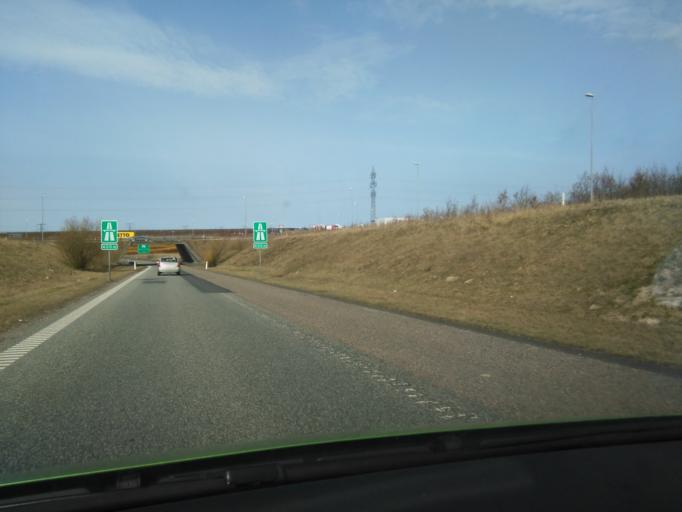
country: DK
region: Central Jutland
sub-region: Arhus Kommune
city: Kolt
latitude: 56.1555
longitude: 10.0717
